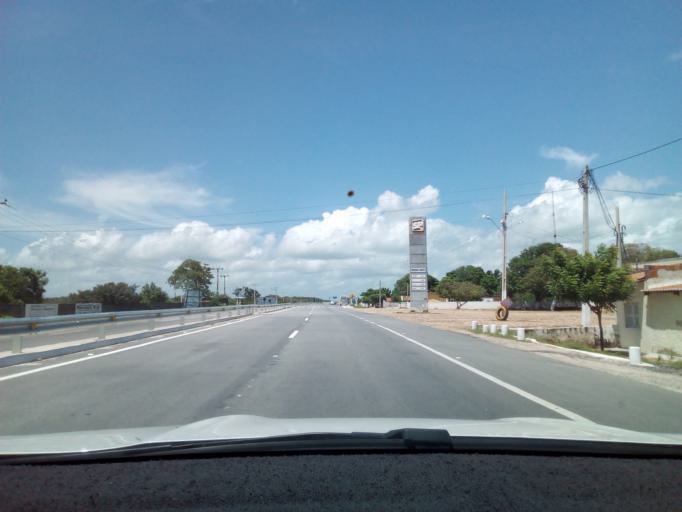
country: BR
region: Ceara
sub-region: Aracati
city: Aracati
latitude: -4.4721
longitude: -37.8012
